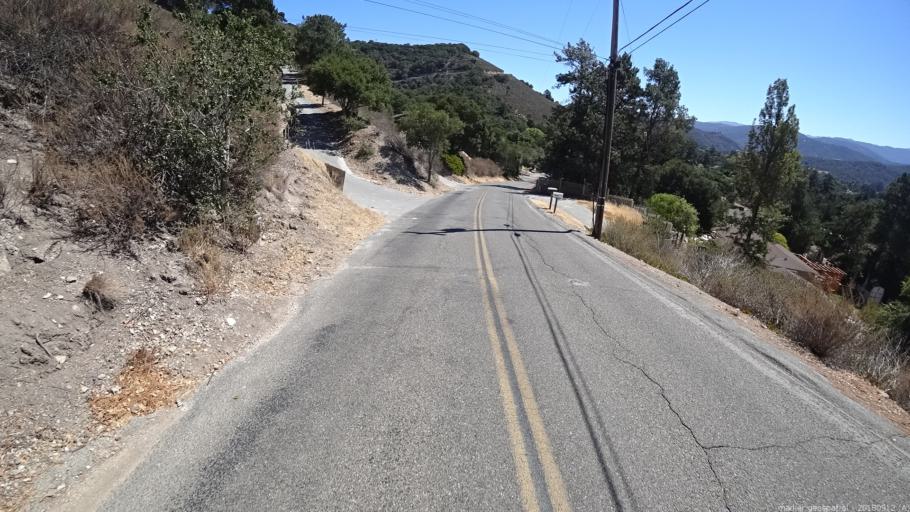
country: US
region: California
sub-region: Monterey County
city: Carmel Valley Village
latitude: 36.4854
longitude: -121.7275
